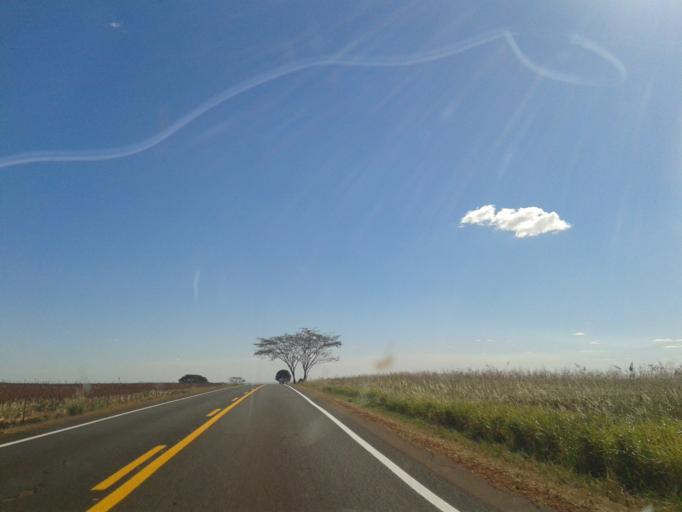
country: BR
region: Minas Gerais
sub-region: Capinopolis
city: Capinopolis
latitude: -18.6846
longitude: -49.5323
